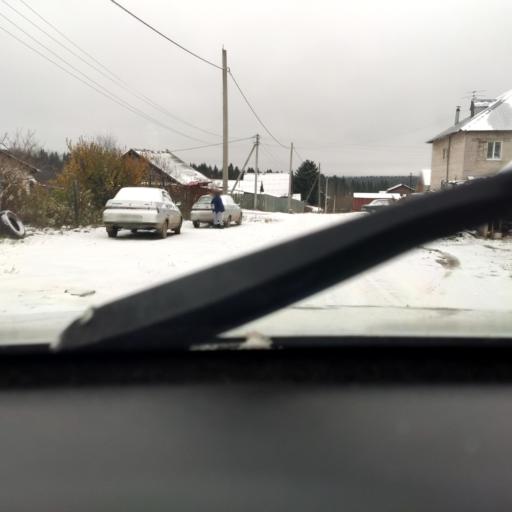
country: RU
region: Perm
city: Ferma
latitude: 57.9882
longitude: 56.3763
